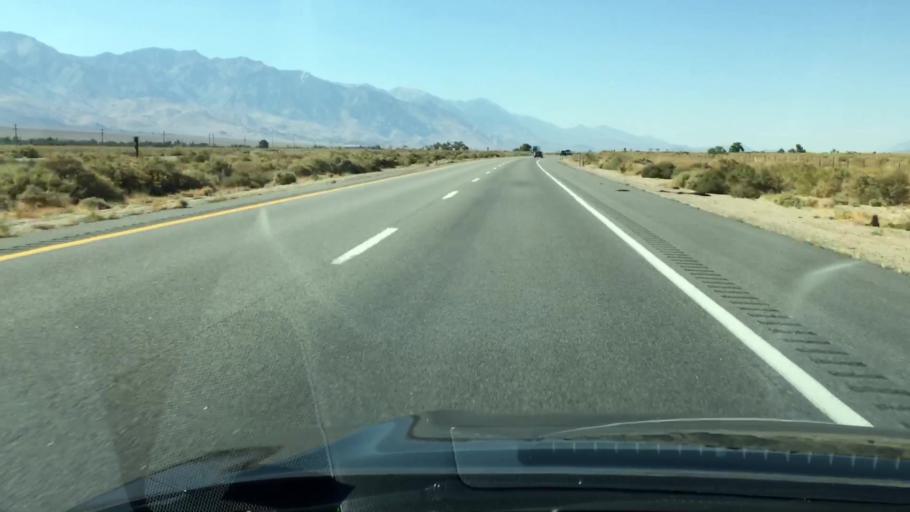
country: US
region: California
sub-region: Inyo County
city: Lone Pine
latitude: 36.7164
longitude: -118.1363
